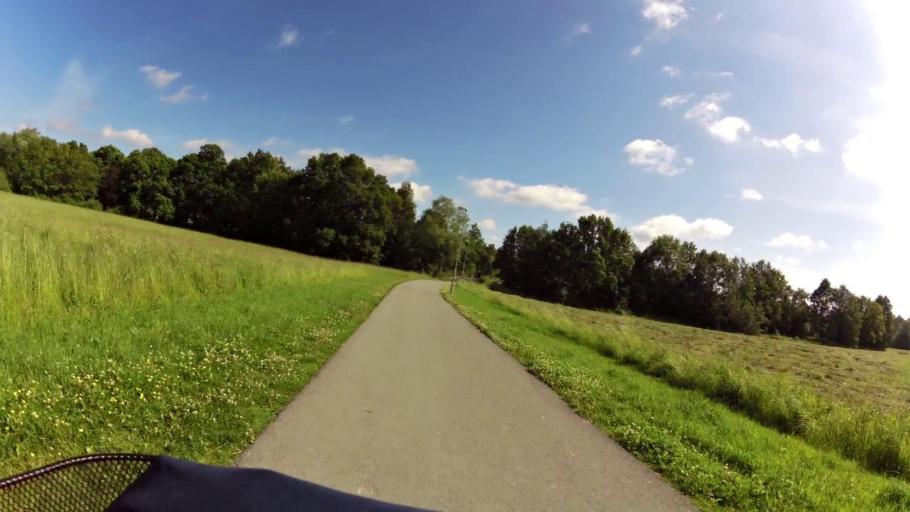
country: SE
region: OEstergoetland
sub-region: Linkopings Kommun
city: Linkoping
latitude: 58.3881
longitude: 15.6338
